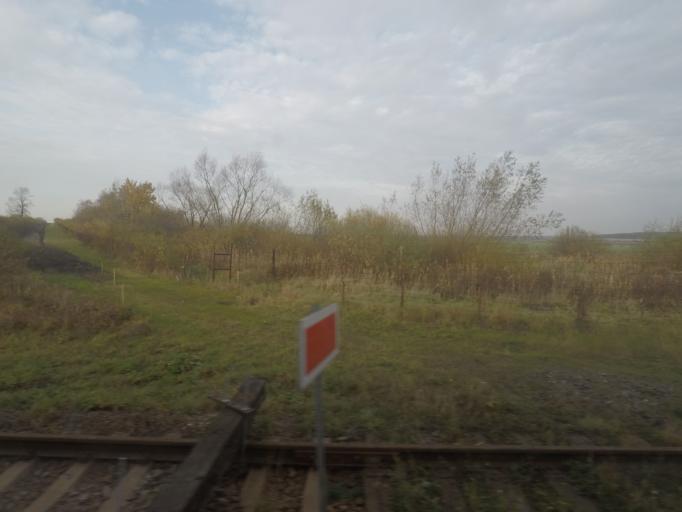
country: PL
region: Subcarpathian Voivodeship
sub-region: Powiat przemyski
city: Medyka
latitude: 49.8052
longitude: 22.9619
